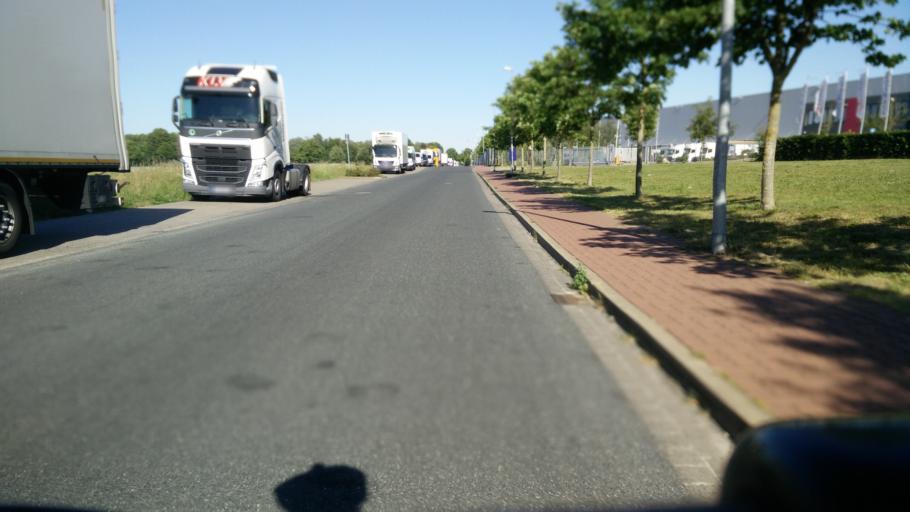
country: DE
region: Lower Saxony
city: Wunstorf
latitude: 52.4085
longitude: 9.4629
